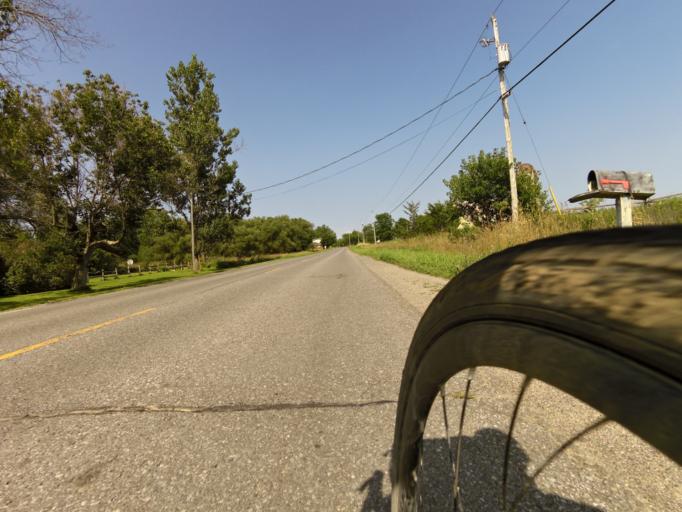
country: CA
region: Ontario
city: Skatepark
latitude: 44.2397
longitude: -76.7388
